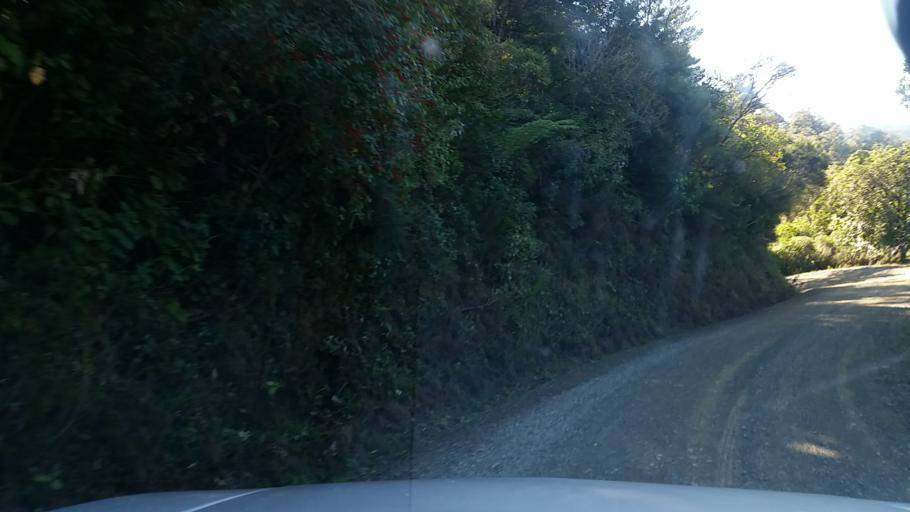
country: NZ
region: Marlborough
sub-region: Marlborough District
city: Picton
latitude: -41.1064
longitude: 173.6532
